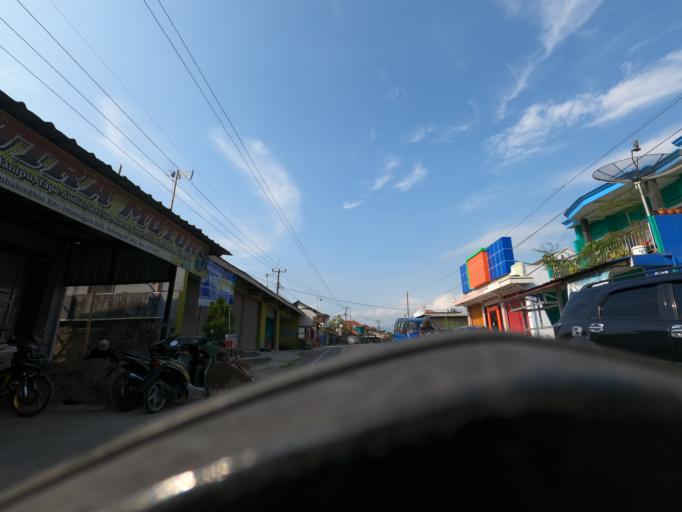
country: ID
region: West Java
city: Lembang
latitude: -6.6490
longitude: 107.7211
